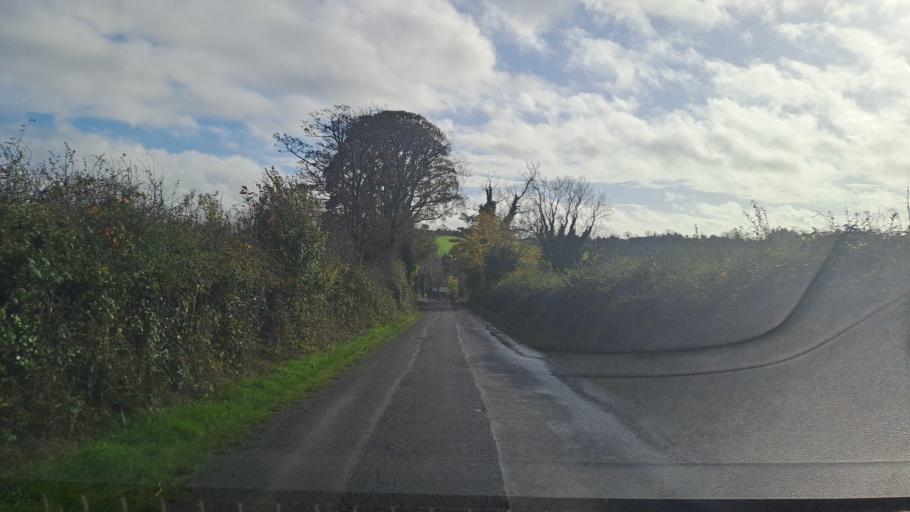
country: IE
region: Ulster
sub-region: An Cabhan
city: Cootehill
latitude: 53.9948
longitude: -7.0264
